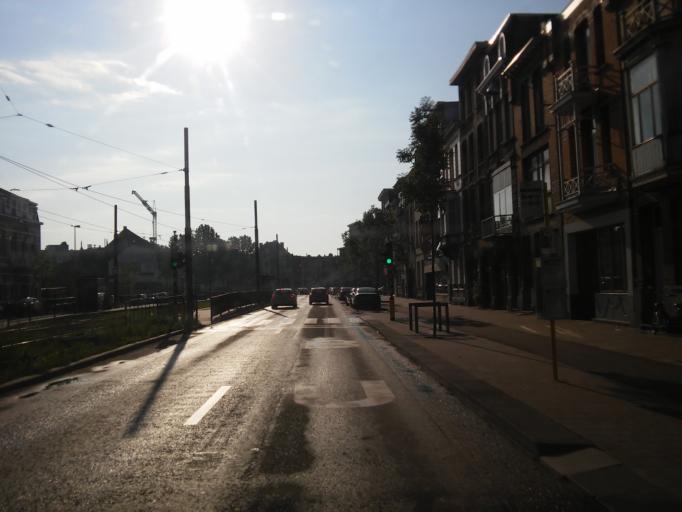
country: BE
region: Flanders
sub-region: Provincie Antwerpen
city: Borsbeek
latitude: 51.2096
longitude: 4.4552
